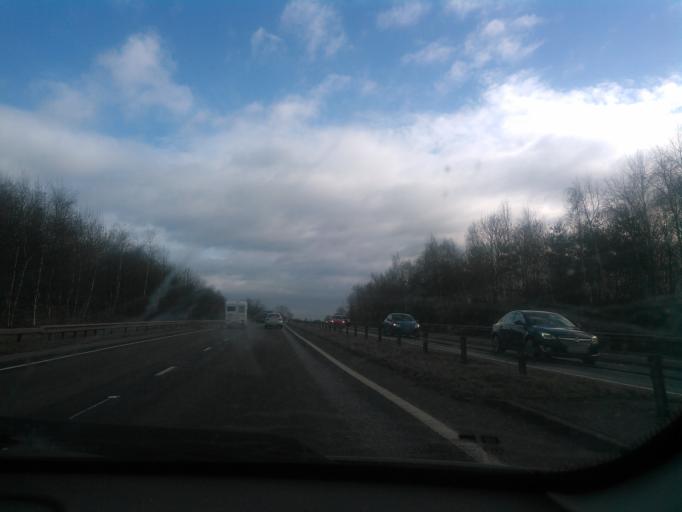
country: GB
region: England
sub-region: Staffordshire
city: Uttoxeter
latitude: 52.8935
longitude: -1.7748
